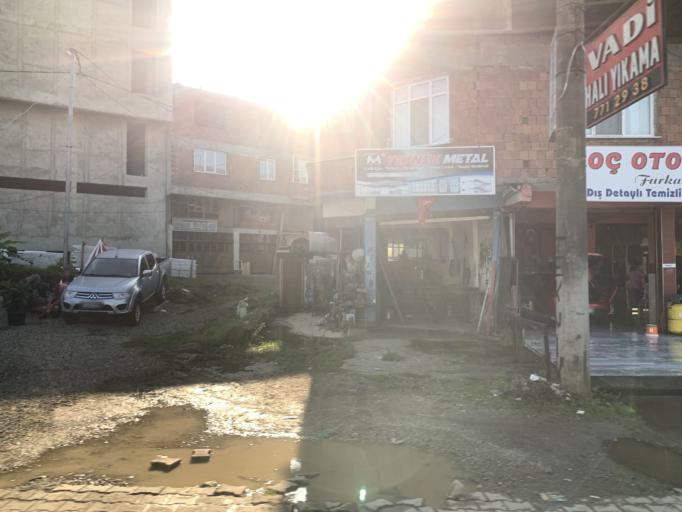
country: TR
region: Trabzon
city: Of
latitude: 40.9392
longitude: 40.2713
